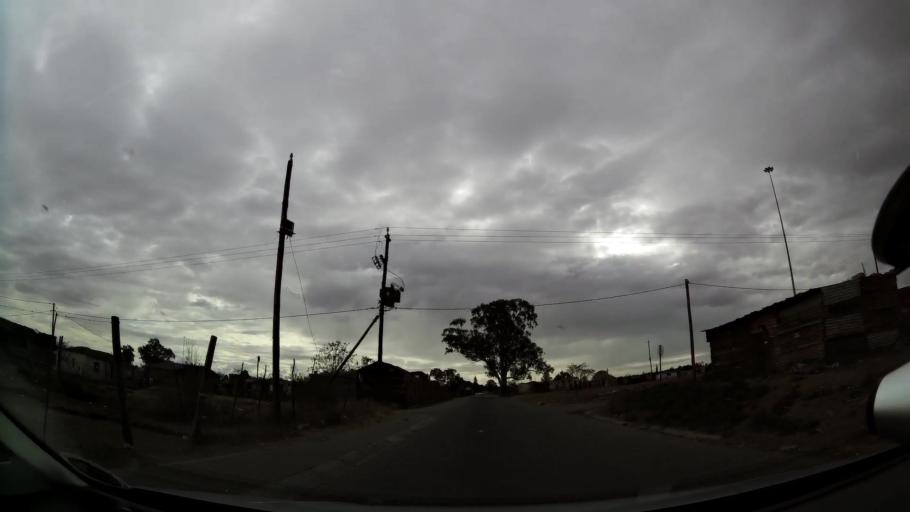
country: ZA
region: Orange Free State
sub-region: Fezile Dabi District Municipality
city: Kroonstad
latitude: -27.6480
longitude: 27.2196
